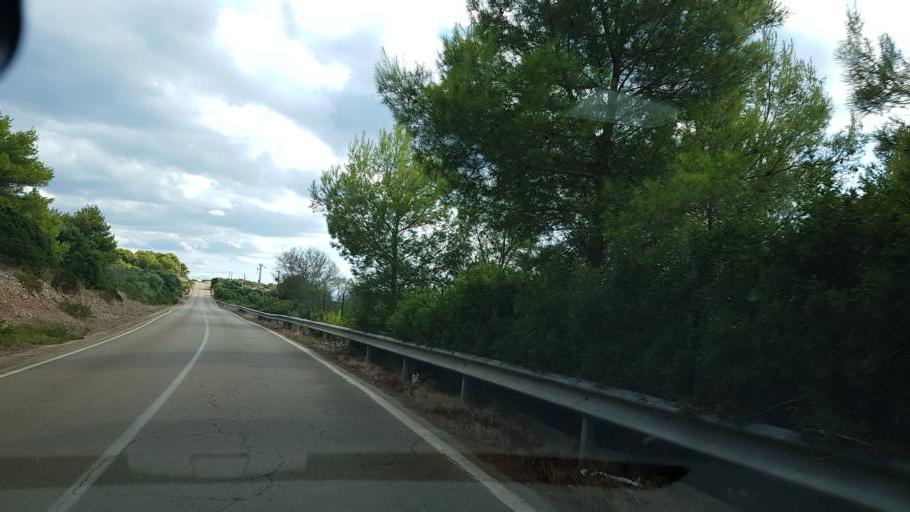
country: IT
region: Apulia
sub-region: Provincia di Lecce
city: Nardo
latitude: 40.1651
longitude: 17.9521
